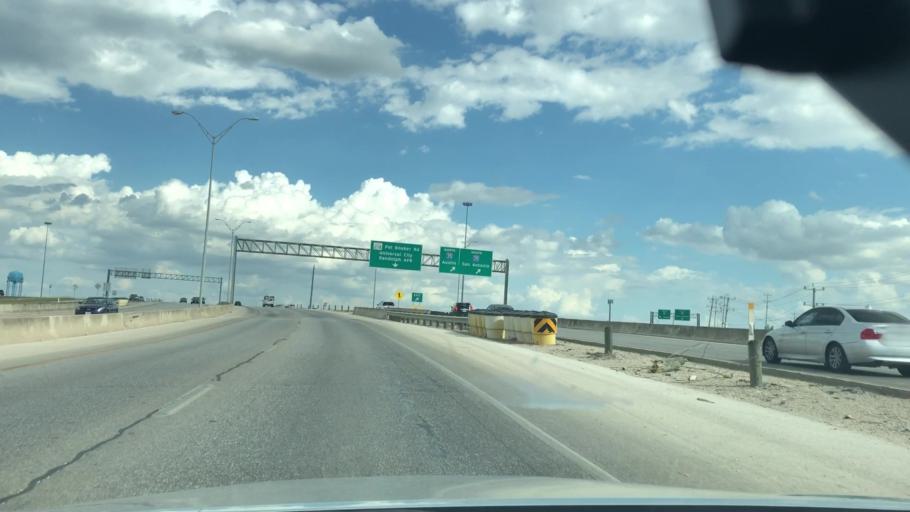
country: US
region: Texas
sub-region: Bexar County
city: Live Oak
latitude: 29.5702
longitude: -98.3366
